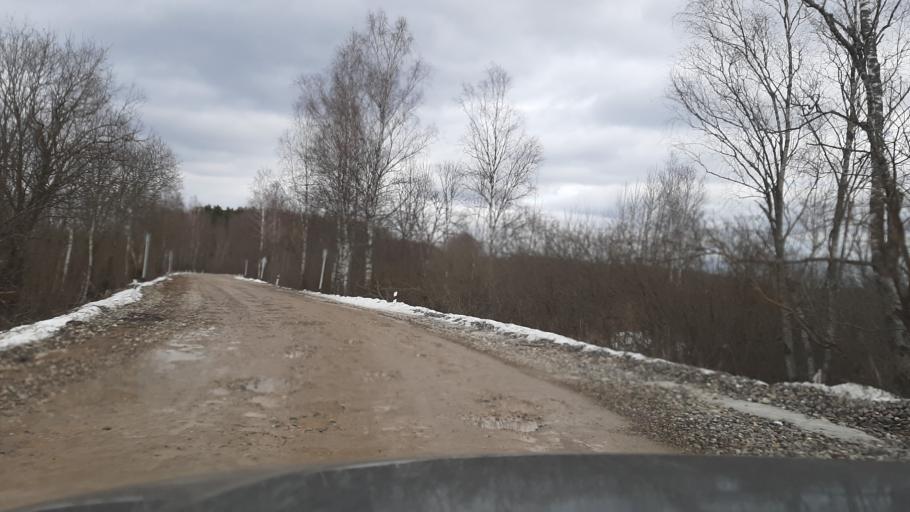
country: RU
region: Ivanovo
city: Teykovo
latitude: 56.8824
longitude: 40.6244
